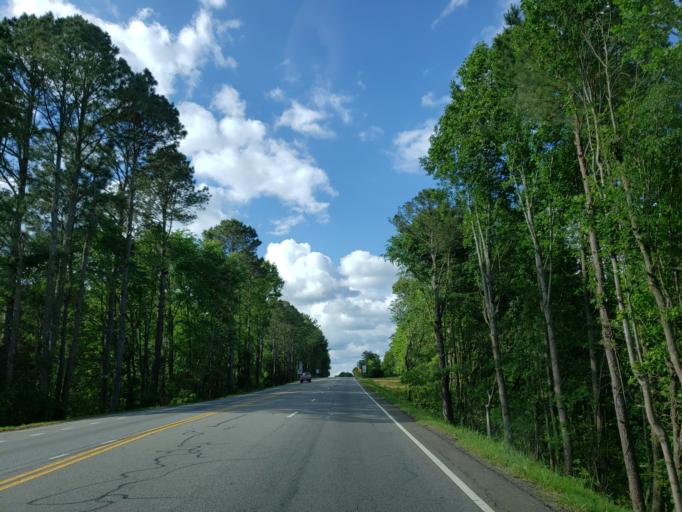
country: US
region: Georgia
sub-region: Bartow County
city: Cartersville
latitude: 34.2455
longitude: -84.8571
